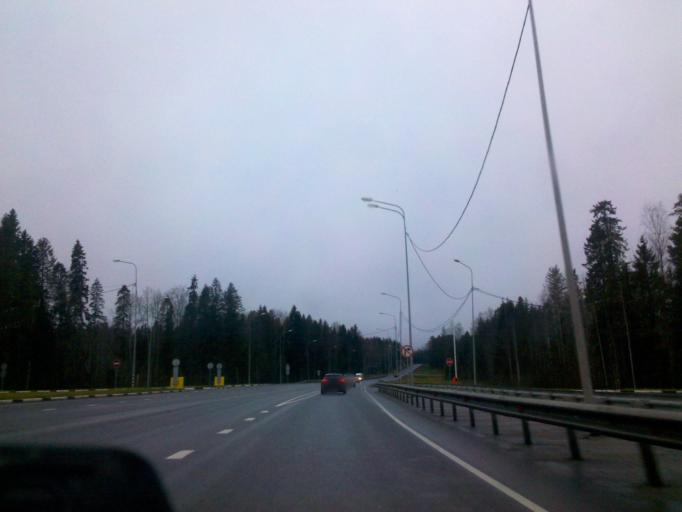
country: RU
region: Republic of Karelia
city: Shuya
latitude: 61.8185
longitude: 34.1308
